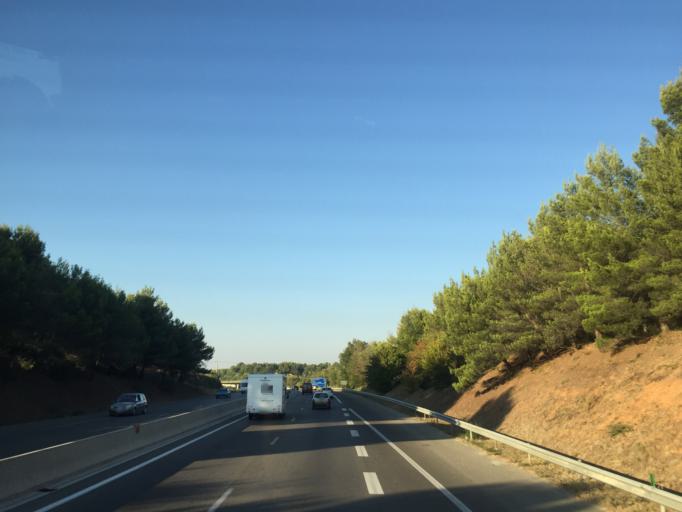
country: FR
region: Provence-Alpes-Cote d'Azur
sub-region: Departement des Bouches-du-Rhone
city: Venelles
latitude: 43.5752
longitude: 5.4715
